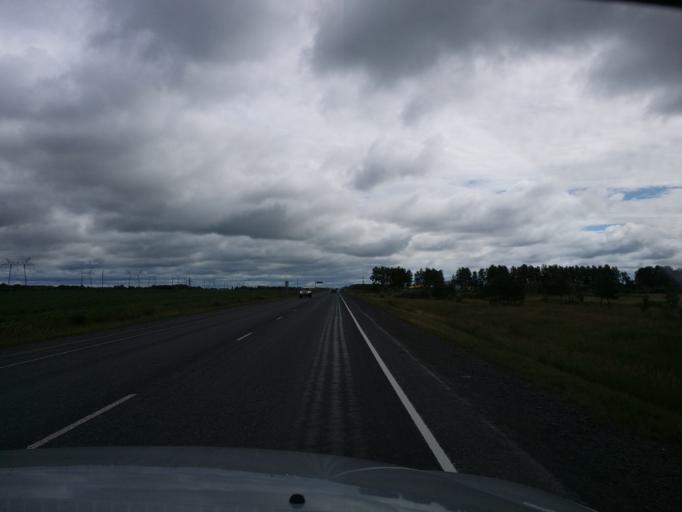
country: RU
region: Tjumen
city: Yarkovo
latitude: 57.1792
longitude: 66.5780
